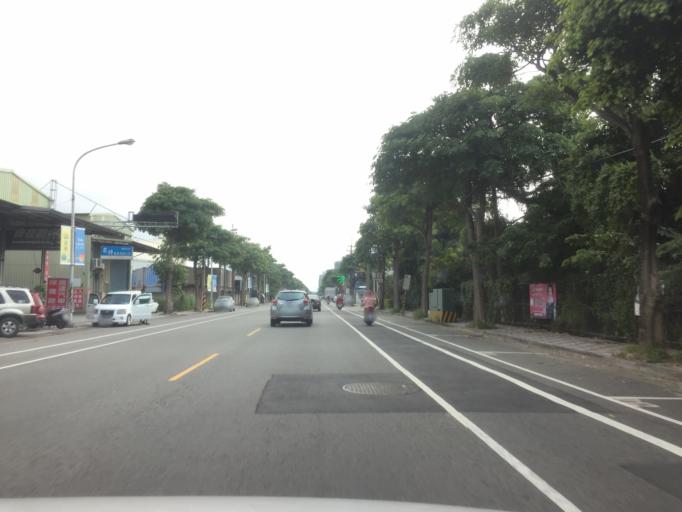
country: TW
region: Taiwan
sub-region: Taoyuan
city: Taoyuan
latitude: 24.9729
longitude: 121.3069
